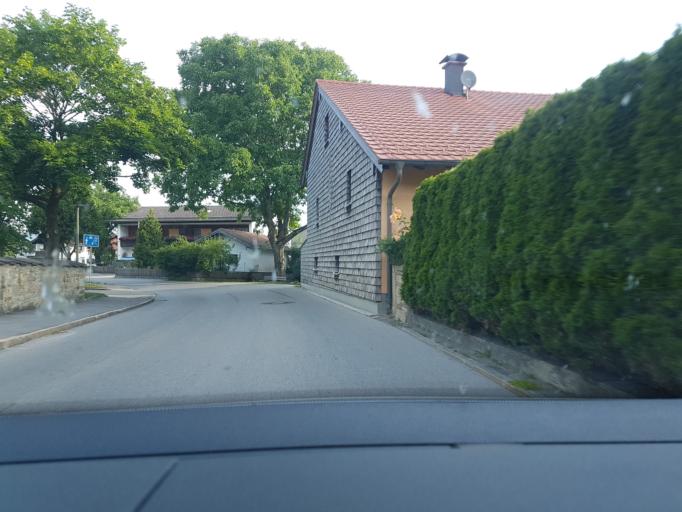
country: DE
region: Bavaria
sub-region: Upper Bavaria
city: Teisendorf
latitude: 47.8504
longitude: 12.7858
